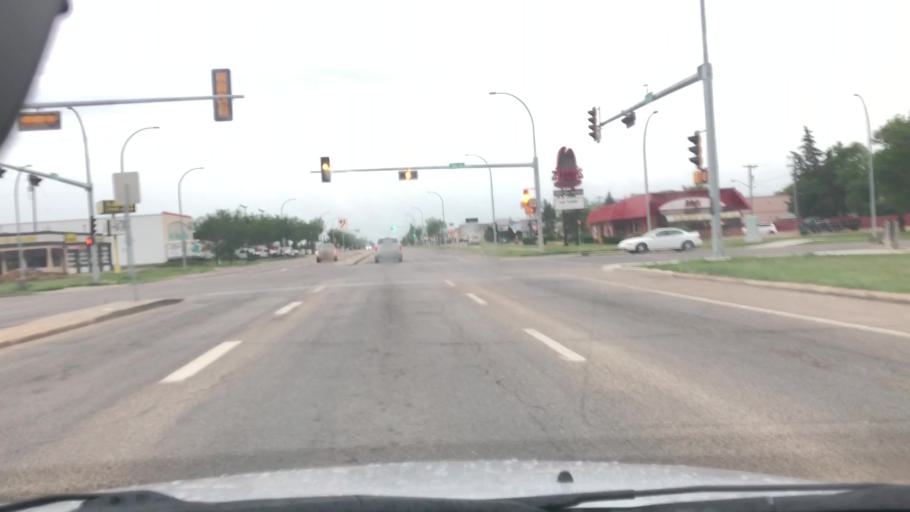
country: CA
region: Alberta
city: St. Albert
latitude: 53.5589
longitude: -113.5909
